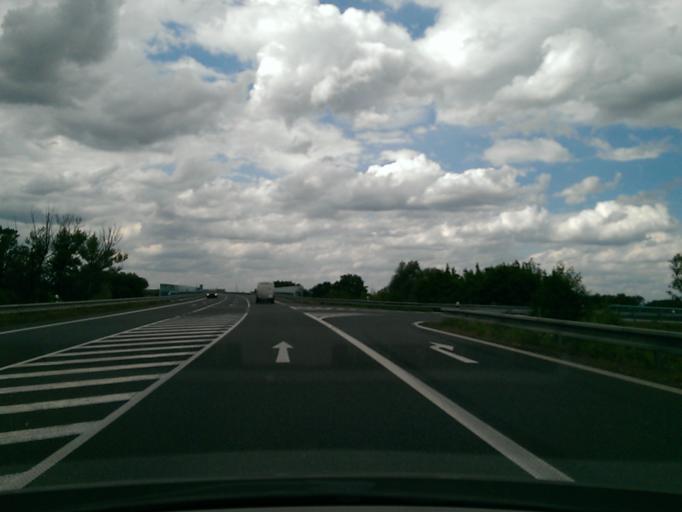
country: CZ
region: Central Bohemia
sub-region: Okres Nymburk
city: Nymburk
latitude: 50.1869
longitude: 15.0771
